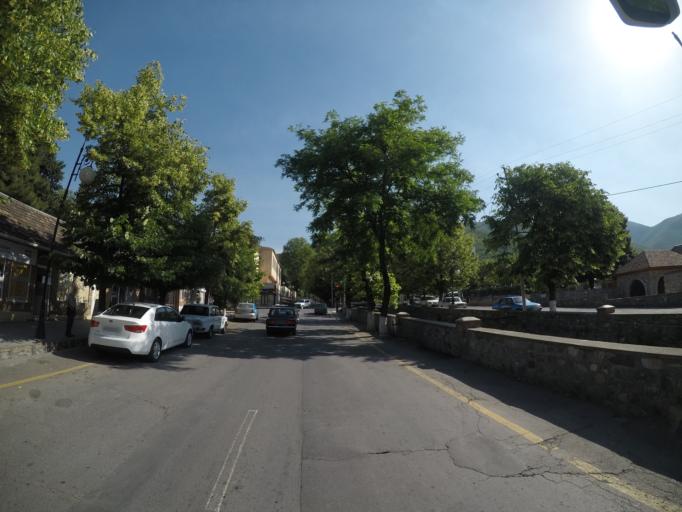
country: AZ
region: Shaki City
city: Sheki
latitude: 41.2030
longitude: 47.1808
